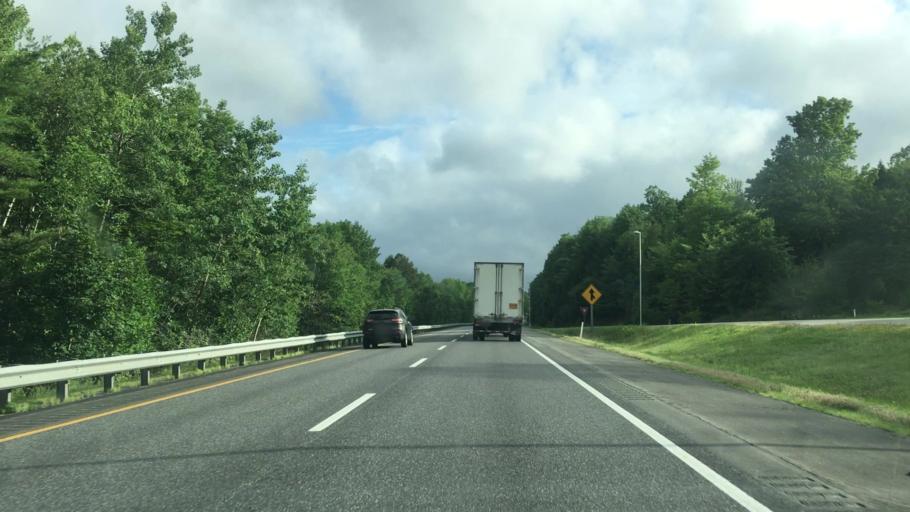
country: US
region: Maine
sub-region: Kennebec County
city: Sidney
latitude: 44.4031
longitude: -69.7516
